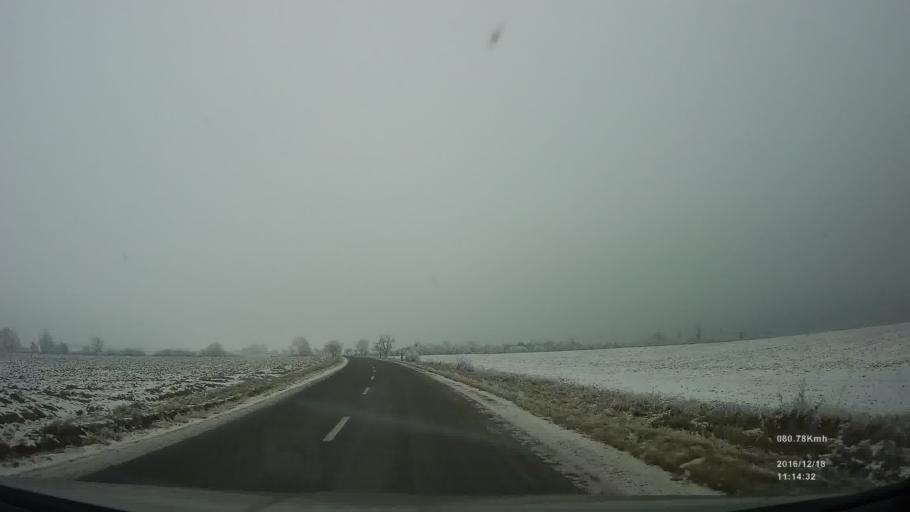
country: SK
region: Presovsky
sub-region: Okres Presov
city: Presov
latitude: 48.8943
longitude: 21.3183
